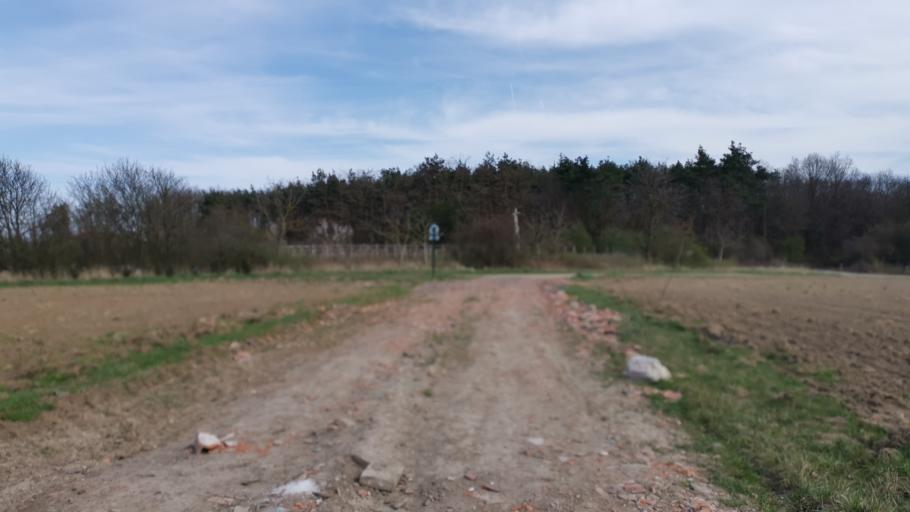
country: SK
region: Trnavsky
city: Gbely
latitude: 48.7033
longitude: 17.1233
